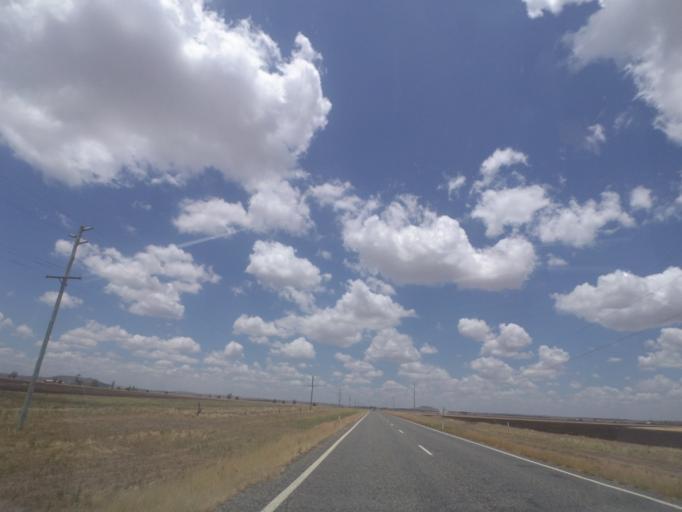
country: AU
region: Queensland
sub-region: Toowoomba
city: Top Camp
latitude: -27.8996
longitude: 151.9759
